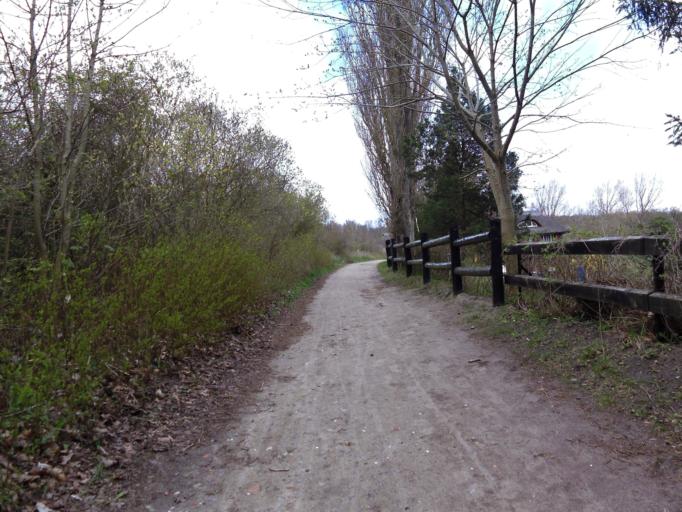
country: DE
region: Mecklenburg-Vorpommern
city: Hiddensee
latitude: 54.5878
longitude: 13.1048
